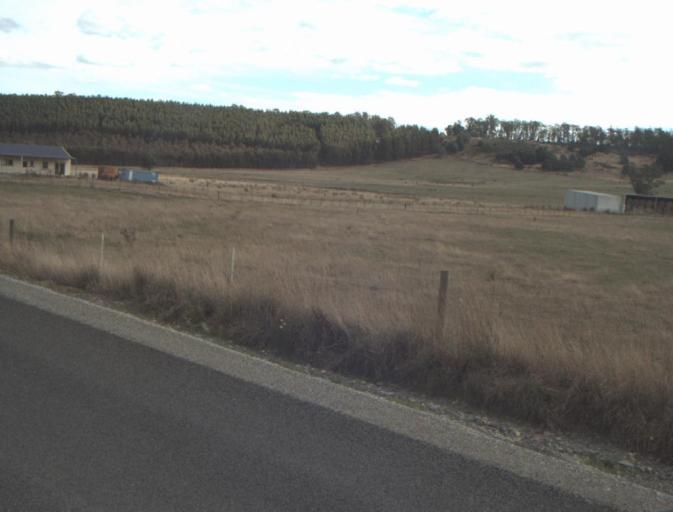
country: AU
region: Tasmania
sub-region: Launceston
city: Mayfield
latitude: -41.1975
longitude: 147.1809
